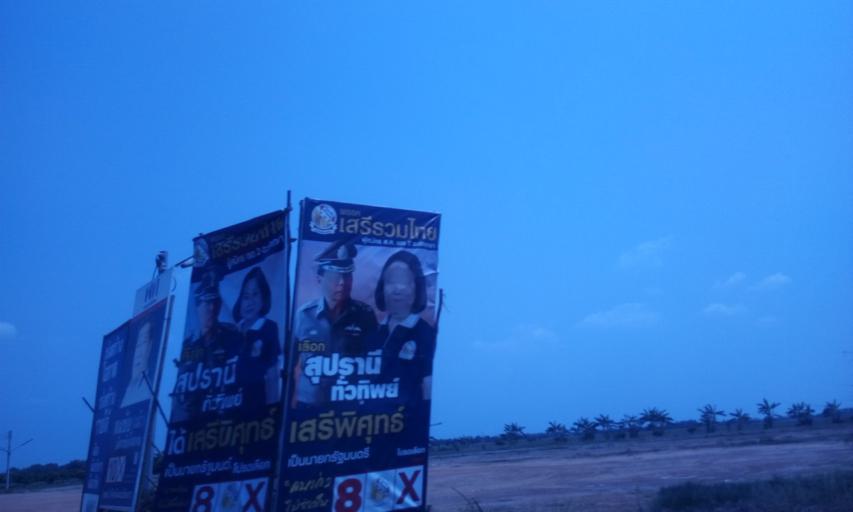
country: TH
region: Chachoengsao
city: Bang Nam Priao
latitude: 13.9626
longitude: 100.9672
